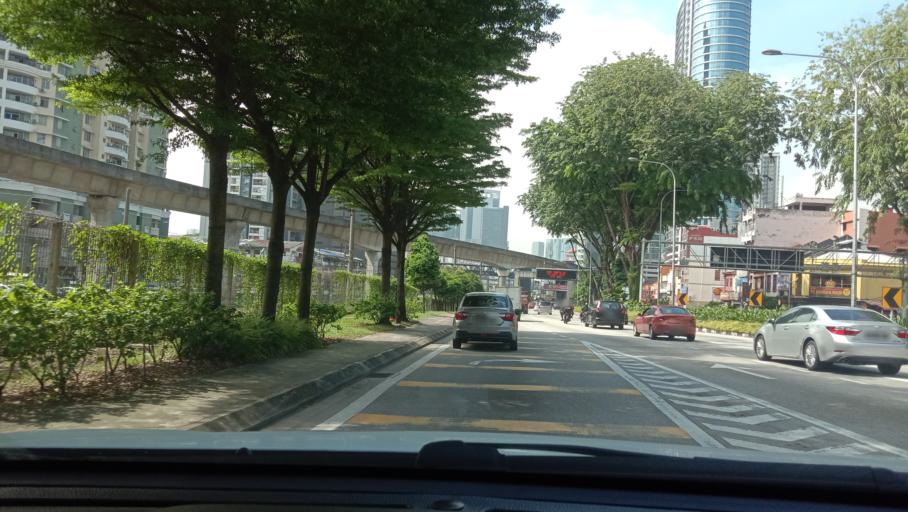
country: MY
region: Kuala Lumpur
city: Kuala Lumpur
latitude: 3.1304
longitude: 101.6814
